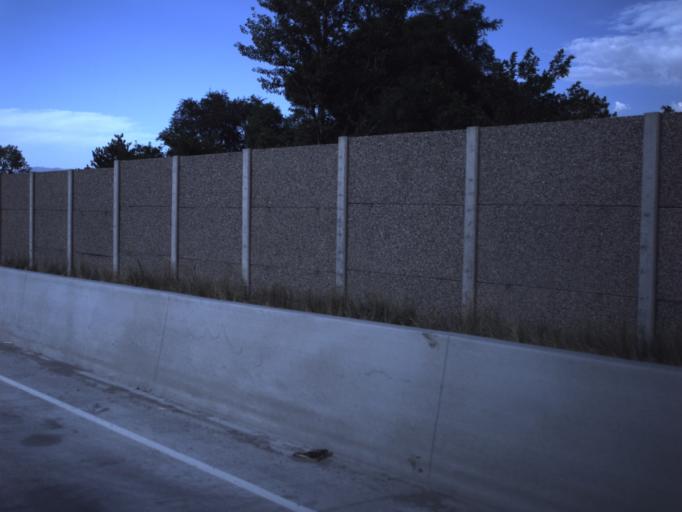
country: US
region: Utah
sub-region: Salt Lake County
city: Taylorsville
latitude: 40.6725
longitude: -111.9523
